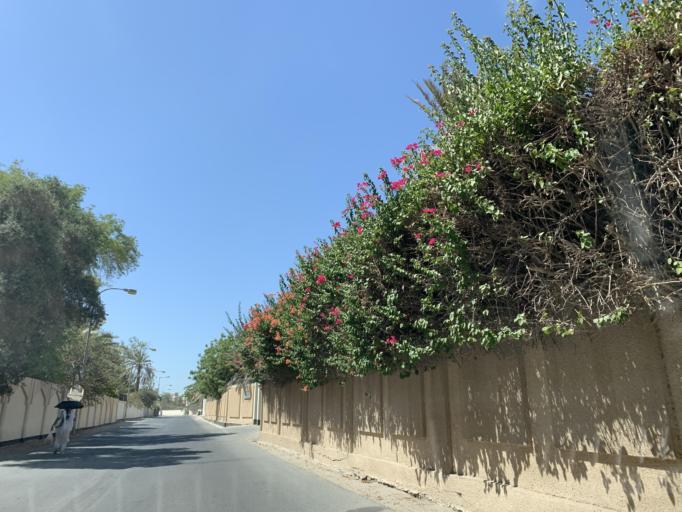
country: BH
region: Manama
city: Jidd Hafs
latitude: 26.2209
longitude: 50.4860
